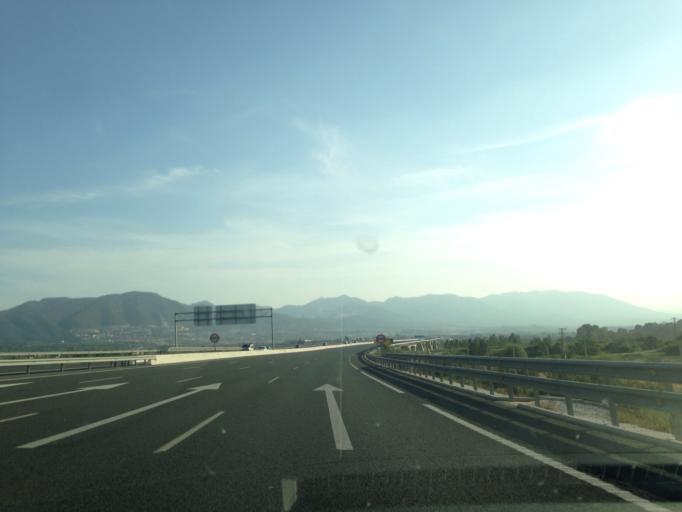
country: ES
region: Andalusia
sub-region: Provincia de Malaga
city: Alhaurin de la Torre
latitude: 36.7000
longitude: -4.5166
